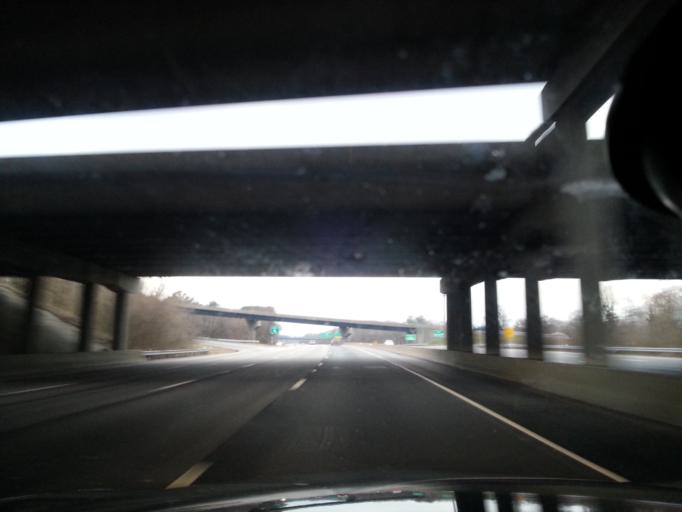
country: US
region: Virginia
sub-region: City of Chesapeake
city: Chesapeake
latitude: 36.8461
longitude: -76.1960
